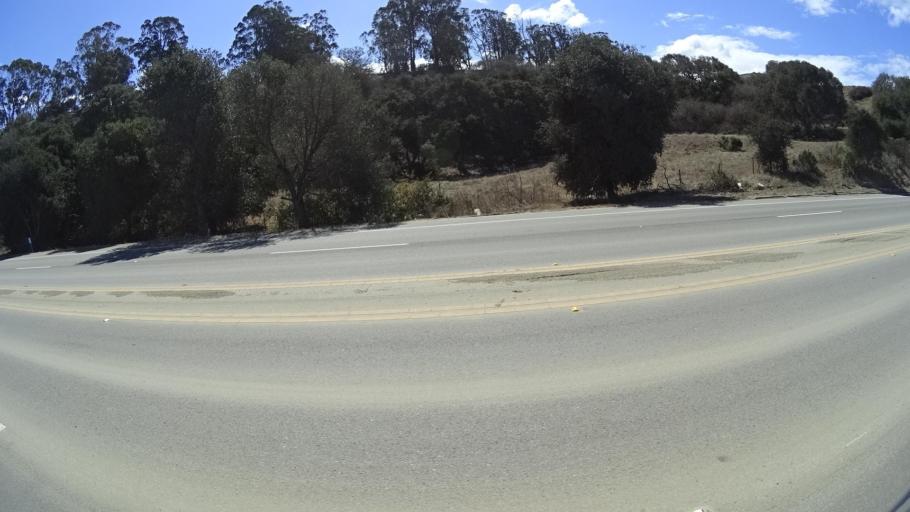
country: US
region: California
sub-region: Monterey County
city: Salinas
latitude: 36.6228
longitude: -121.6739
